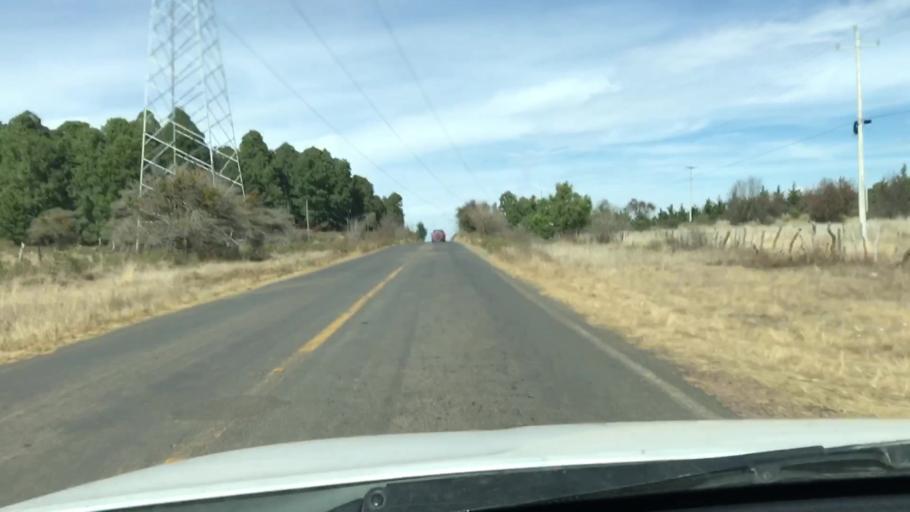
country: MX
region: Jalisco
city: Chiquilistlan
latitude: 20.1046
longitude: -103.7182
